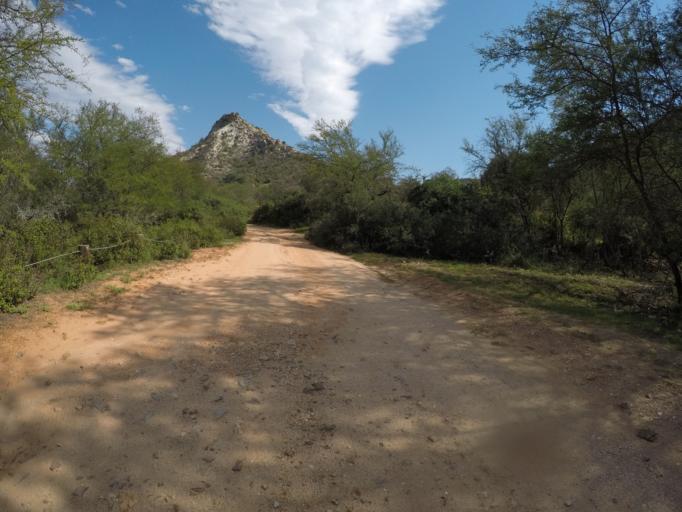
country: ZA
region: Eastern Cape
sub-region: Cacadu District Municipality
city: Kareedouw
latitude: -33.6576
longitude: 24.4325
